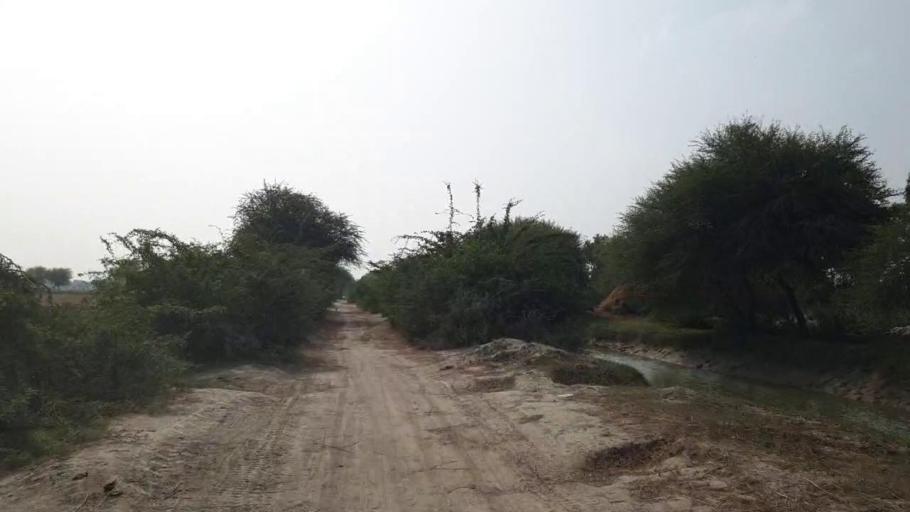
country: PK
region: Sindh
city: Kario
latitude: 24.7823
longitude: 68.5637
